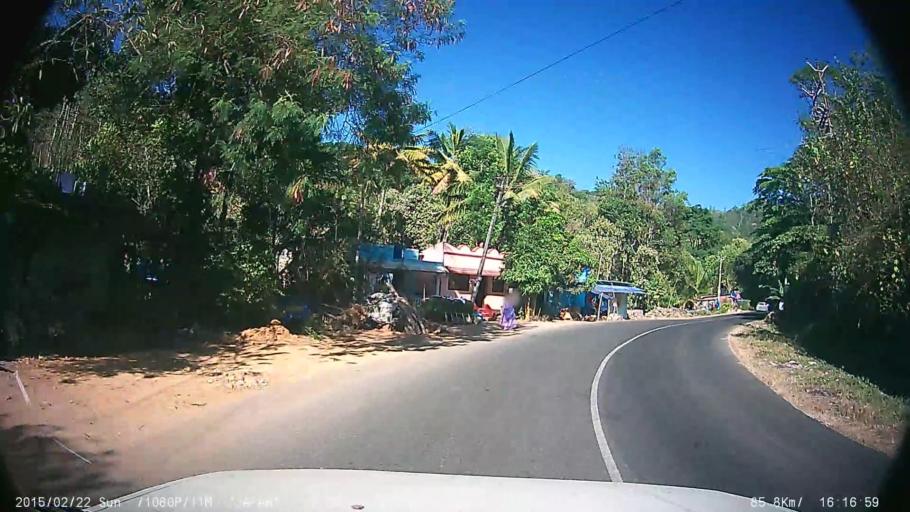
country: IN
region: Tamil Nadu
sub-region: Theni
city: Gudalur
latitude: 9.5834
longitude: 77.1143
